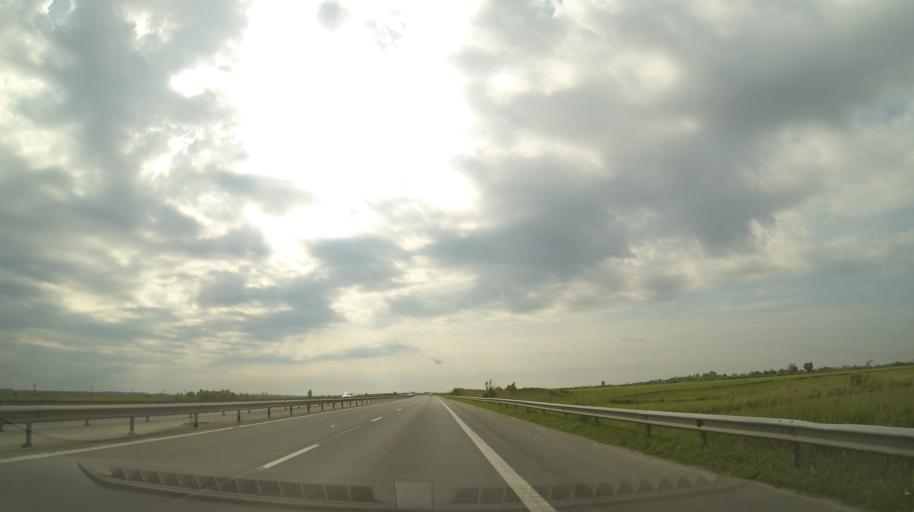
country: RO
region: Dambovita
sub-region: Comuna Mogosani
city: Zavoiu
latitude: 44.6371
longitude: 25.4046
